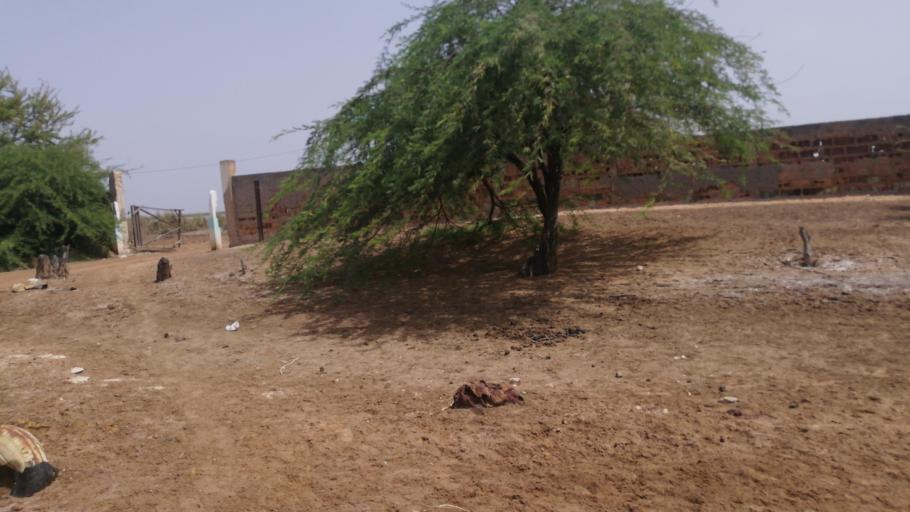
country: SN
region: Saint-Louis
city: Saint-Louis
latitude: 16.3587
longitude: -16.2742
